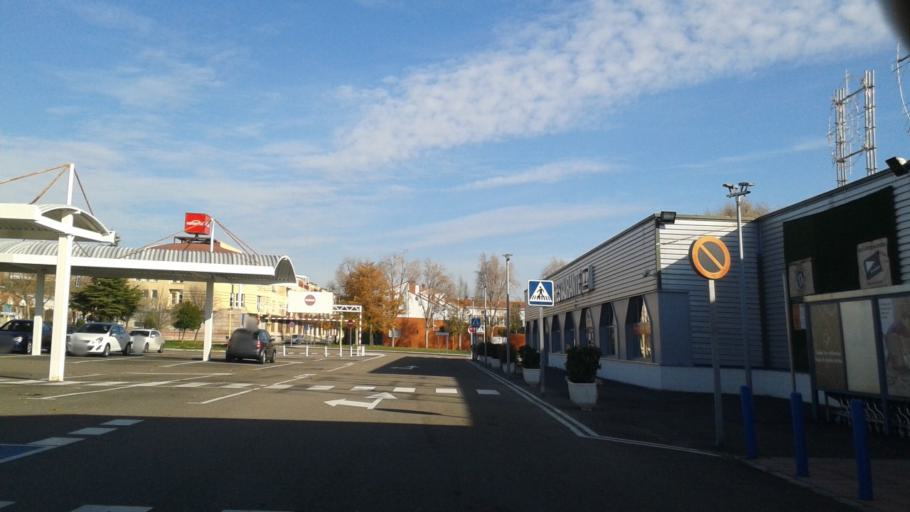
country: ES
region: Castille and Leon
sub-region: Provincia de Valladolid
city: Arroyo
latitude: 41.6231
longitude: -4.7691
